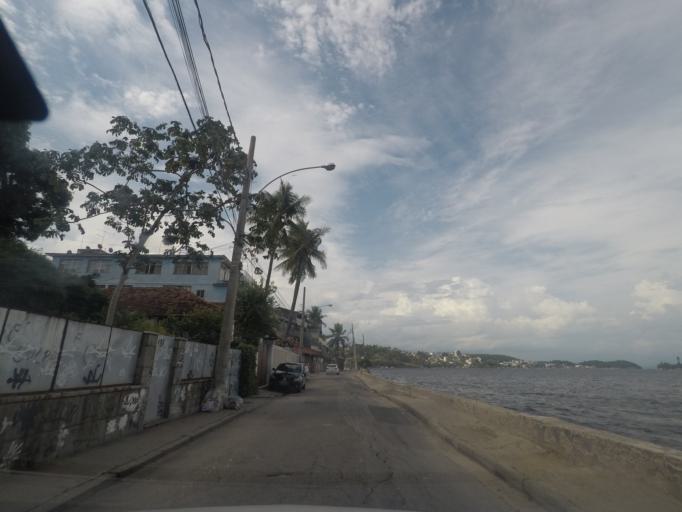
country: BR
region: Rio de Janeiro
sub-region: Rio De Janeiro
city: Rio de Janeiro
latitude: -22.8085
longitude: -43.1776
